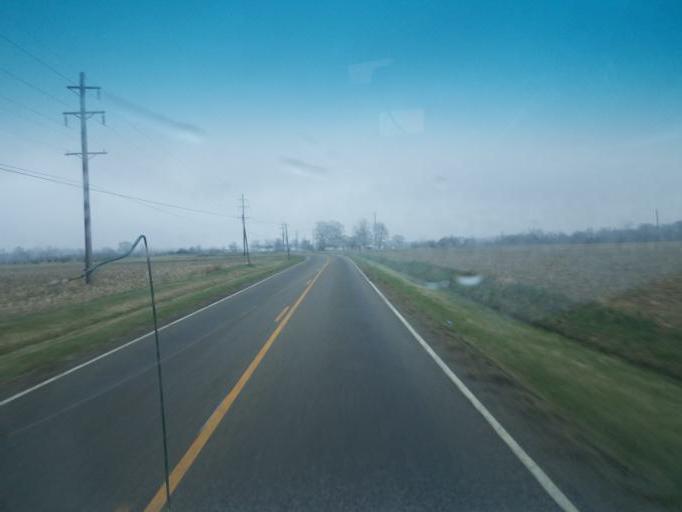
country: US
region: Ohio
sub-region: Defiance County
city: Hicksville
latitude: 41.3403
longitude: -84.7670
